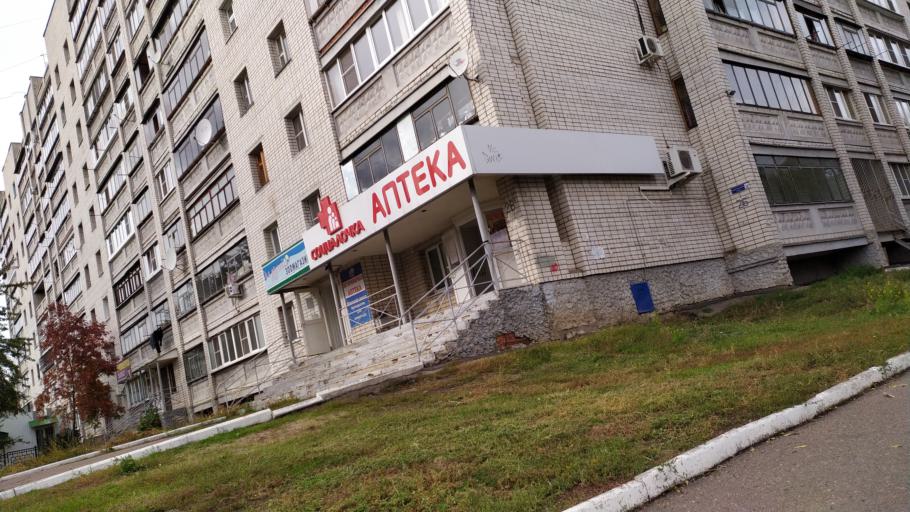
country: RU
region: Kursk
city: Kursk
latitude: 51.6493
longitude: 36.1463
